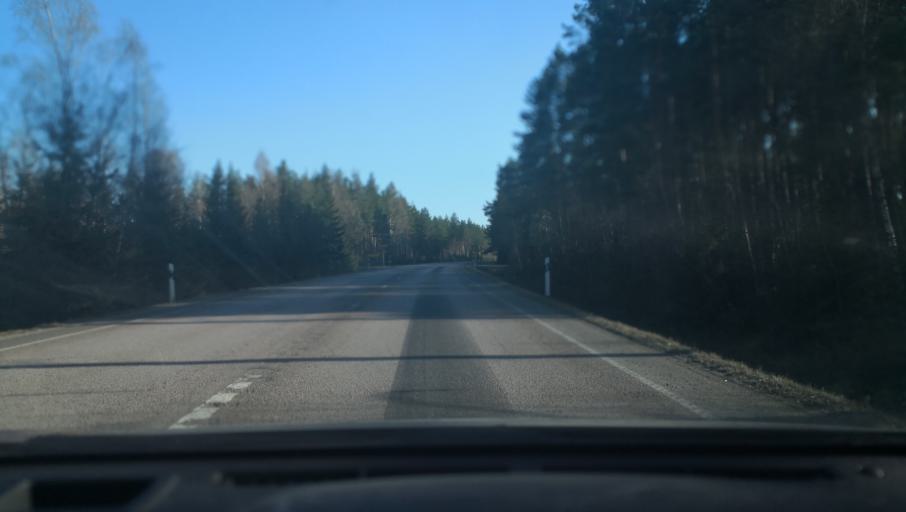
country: SE
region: Uppsala
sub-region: Heby Kommun
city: Heby
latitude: 59.9762
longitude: 16.8369
